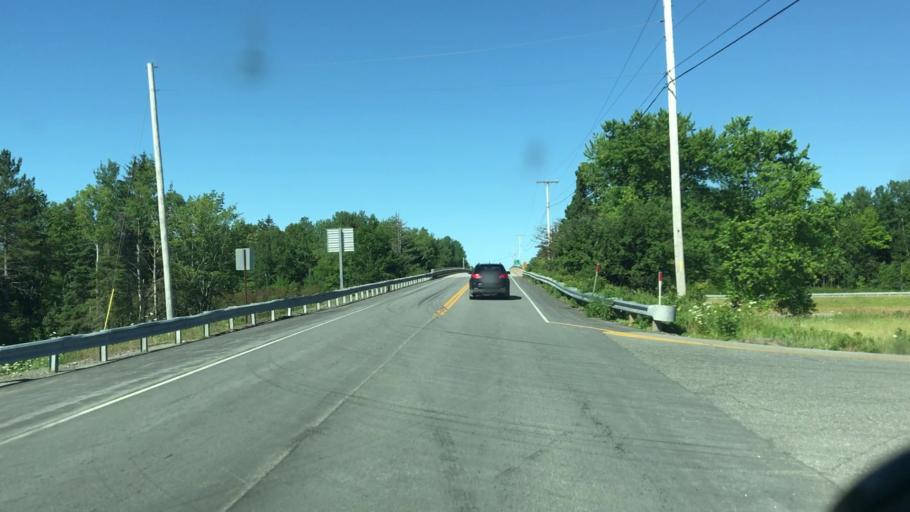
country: US
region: Maine
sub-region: Penobscot County
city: Howland
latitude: 45.2365
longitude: -68.6754
